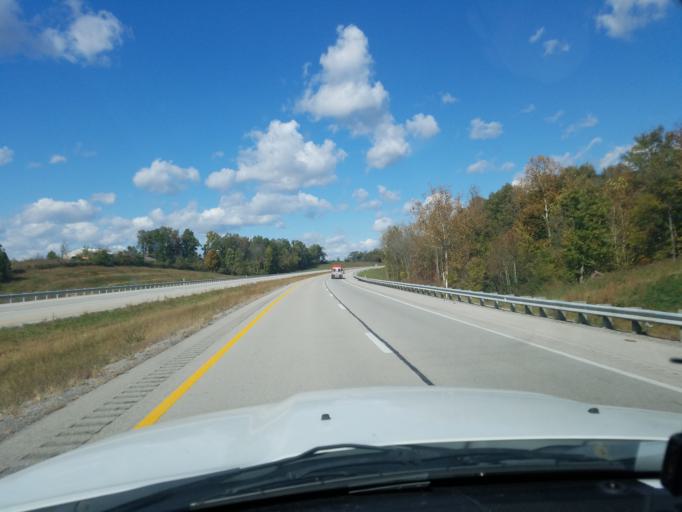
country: US
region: Kentucky
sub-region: Ohio County
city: Hartford
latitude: 37.4818
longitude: -86.9058
